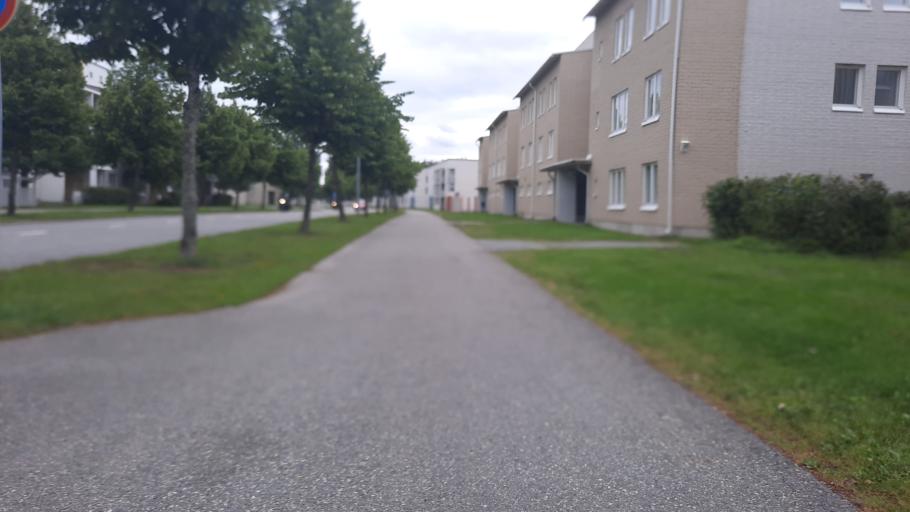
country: FI
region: North Karelia
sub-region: Joensuu
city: Joensuu
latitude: 62.6246
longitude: 29.8551
